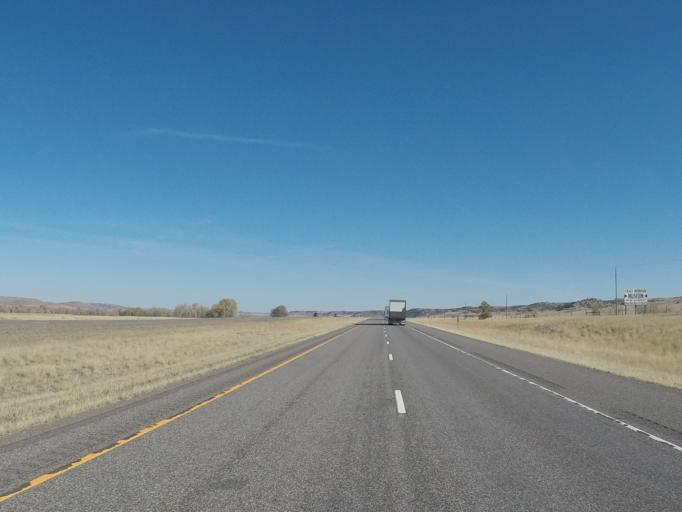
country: US
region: Montana
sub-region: Sweet Grass County
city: Big Timber
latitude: 45.7498
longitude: -110.1636
